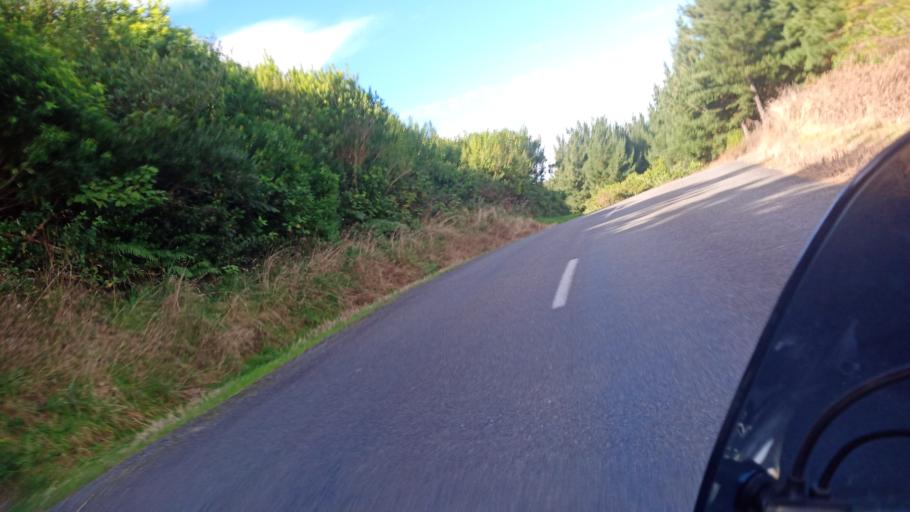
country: NZ
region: Hawke's Bay
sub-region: Wairoa District
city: Wairoa
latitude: -39.0044
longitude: 177.0900
